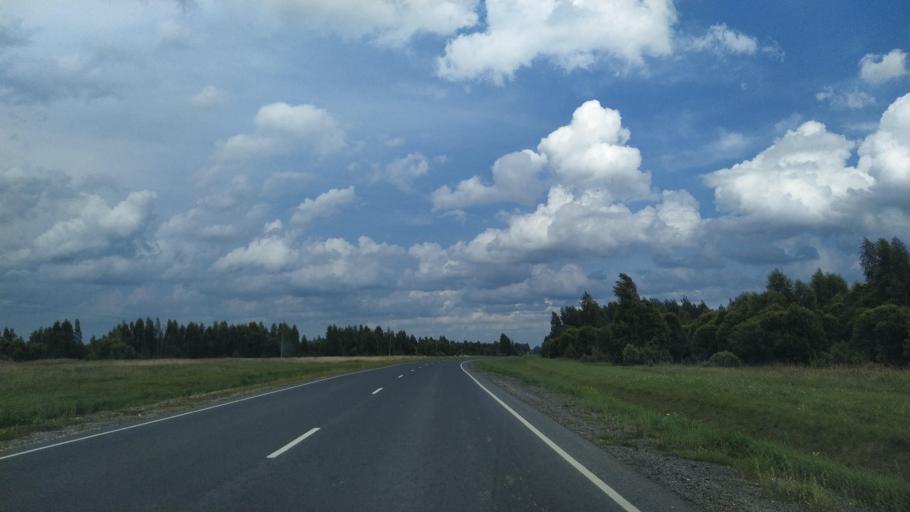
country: RU
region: Pskov
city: Dno
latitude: 58.0648
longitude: 30.0330
